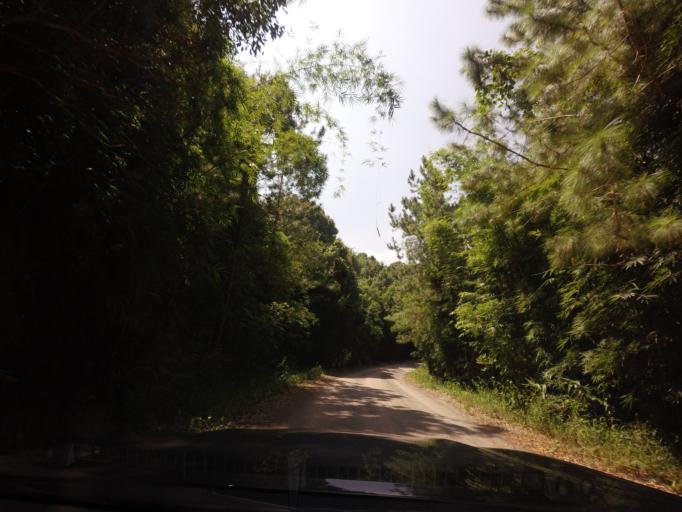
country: TH
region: Loei
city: Na Haeo
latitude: 17.5067
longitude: 100.9407
